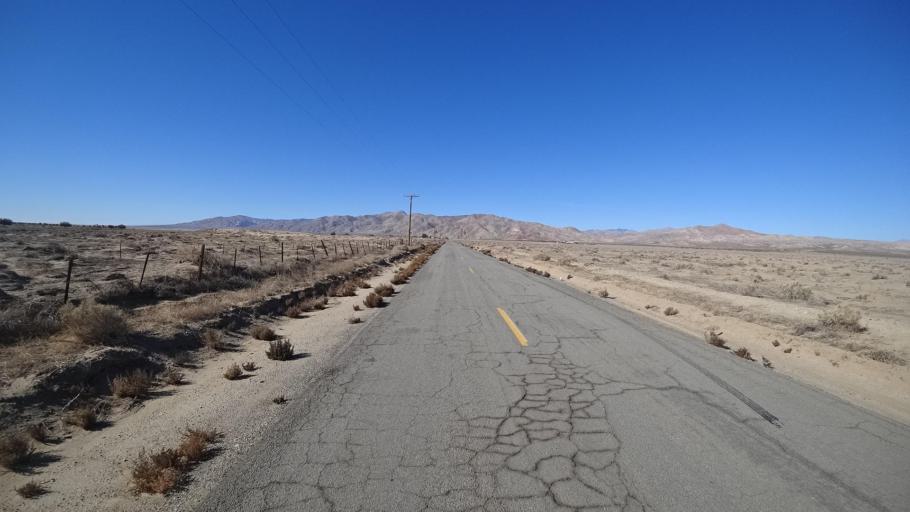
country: US
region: California
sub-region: Kern County
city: California City
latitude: 35.2868
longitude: -117.9717
